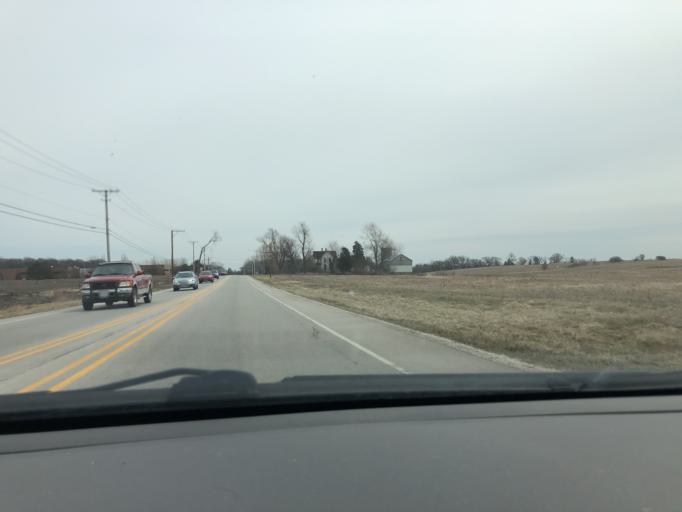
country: US
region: Illinois
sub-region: Kane County
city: Sleepy Hollow
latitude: 42.0673
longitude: -88.3408
